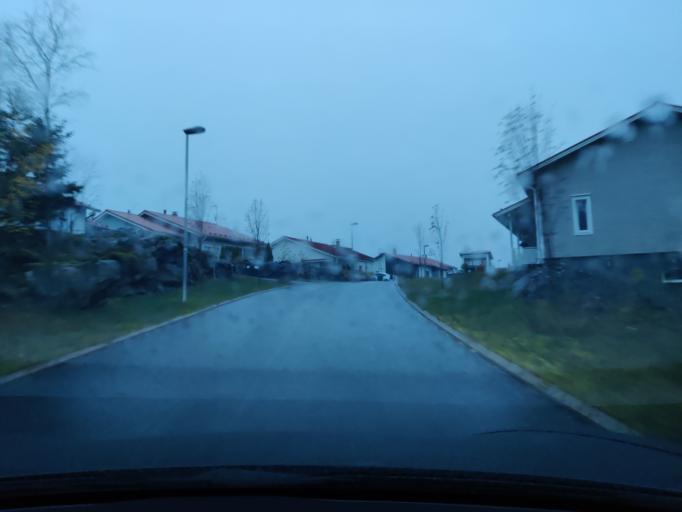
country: FI
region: Northern Savo
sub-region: Kuopio
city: Kuopio
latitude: 62.8264
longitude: 27.7231
